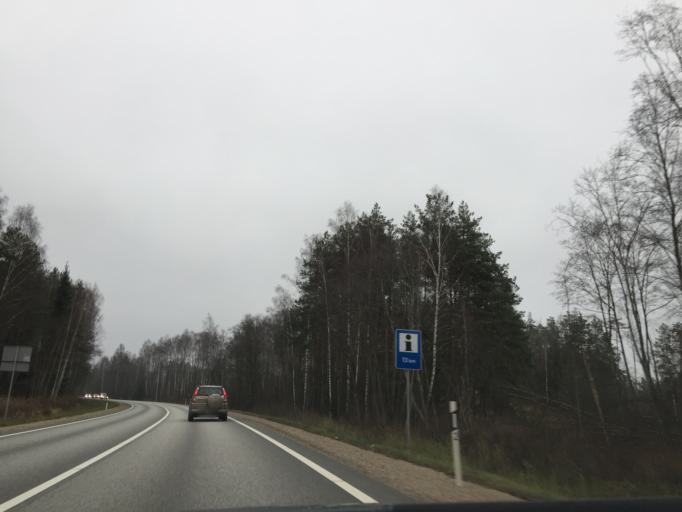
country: LV
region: Pargaujas
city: Stalbe
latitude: 57.2985
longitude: 24.9251
